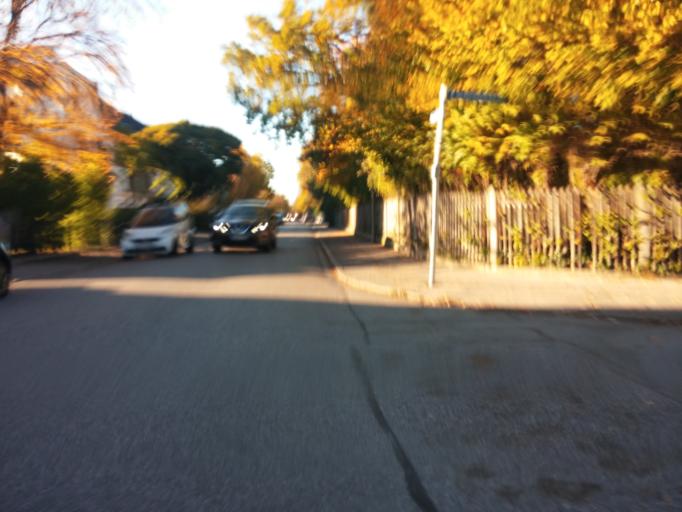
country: DE
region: Bavaria
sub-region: Upper Bavaria
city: Haar
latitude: 48.1074
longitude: 11.7097
